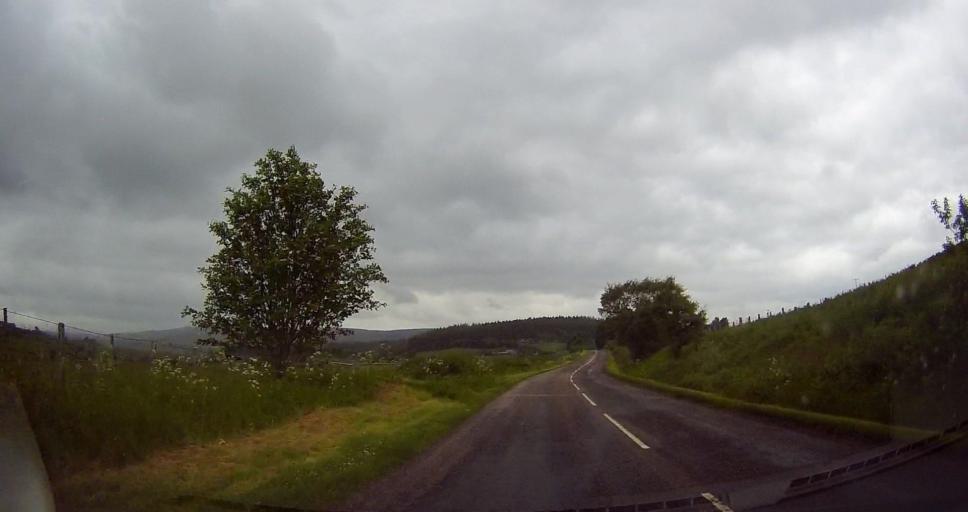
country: GB
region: Scotland
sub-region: Highland
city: Alness
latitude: 58.0184
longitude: -4.3628
